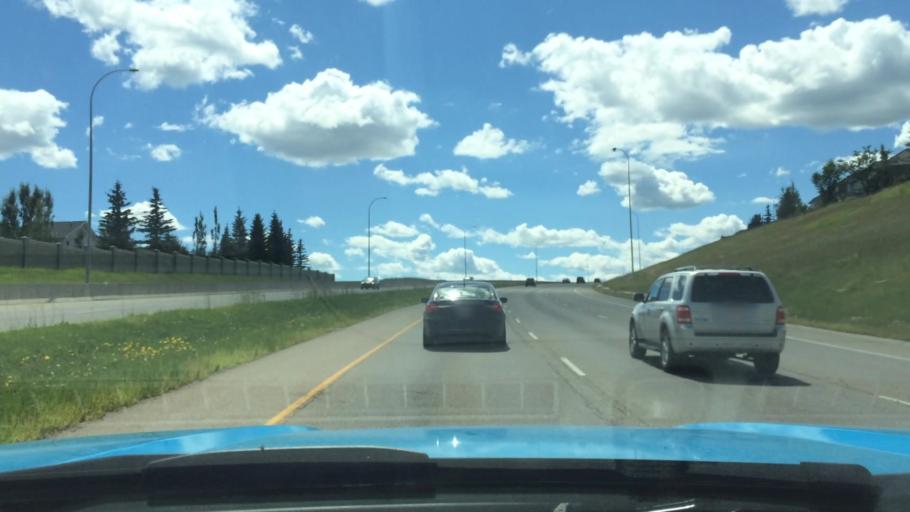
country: CA
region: Alberta
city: Calgary
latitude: 51.1339
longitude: -114.1229
